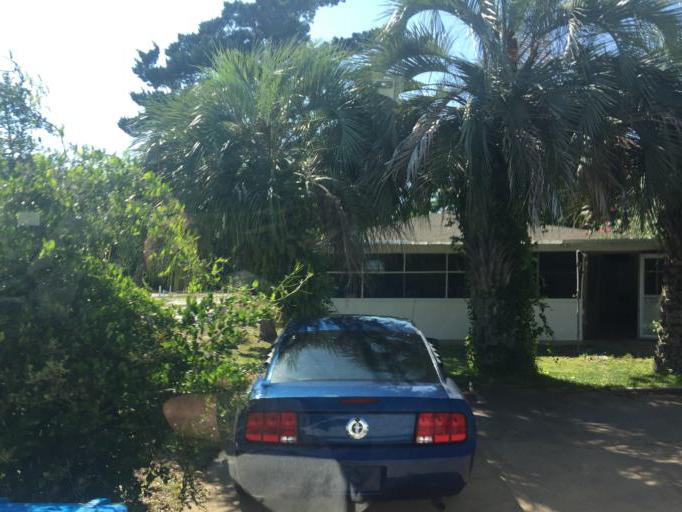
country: US
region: Florida
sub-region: Bay County
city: Panama City Beach
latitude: 30.2043
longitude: -85.8471
